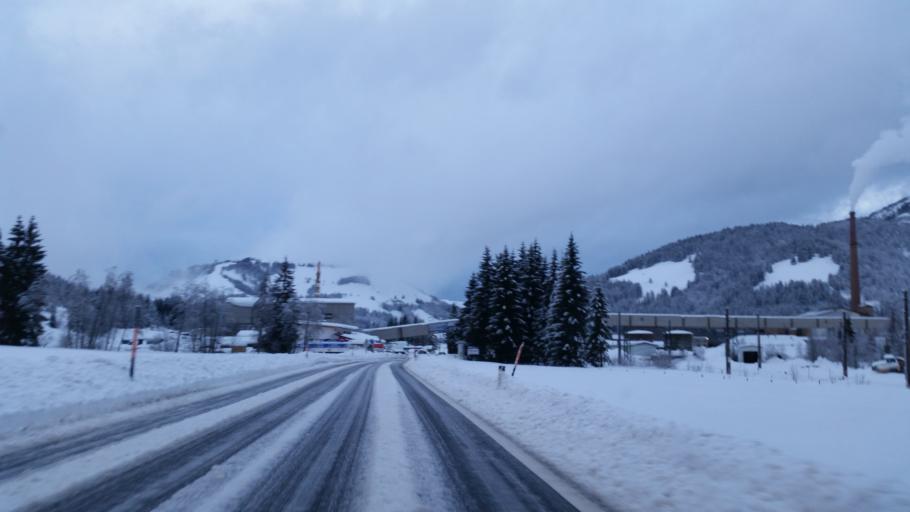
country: AT
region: Tyrol
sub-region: Politischer Bezirk Kitzbuhel
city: Hochfilzen
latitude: 47.4627
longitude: 12.6335
